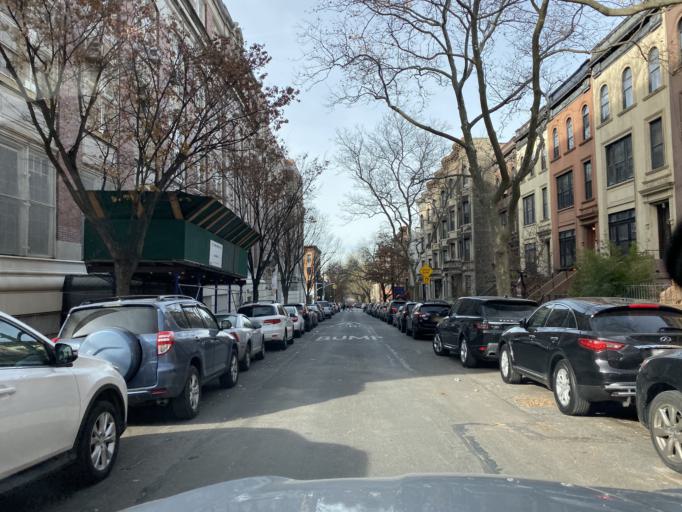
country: US
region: New York
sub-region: Kings County
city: Brooklyn
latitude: 40.6693
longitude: -73.9778
